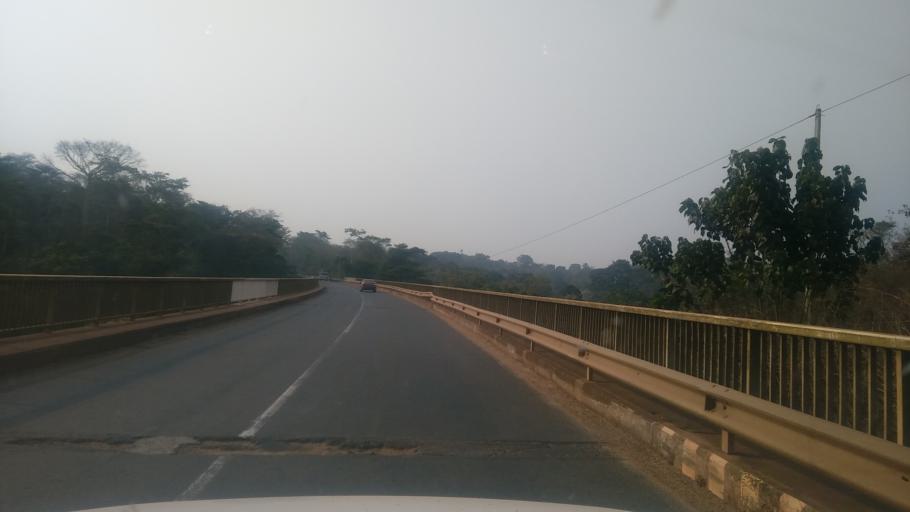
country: CM
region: West
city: Tonga
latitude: 5.0547
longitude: 10.6980
